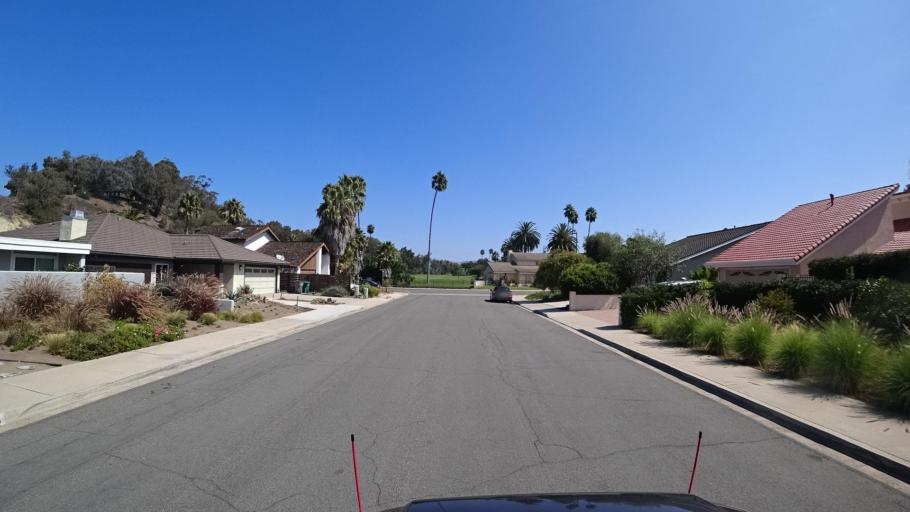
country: US
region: California
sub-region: San Diego County
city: Fairbanks Ranch
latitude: 32.9940
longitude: -117.2105
